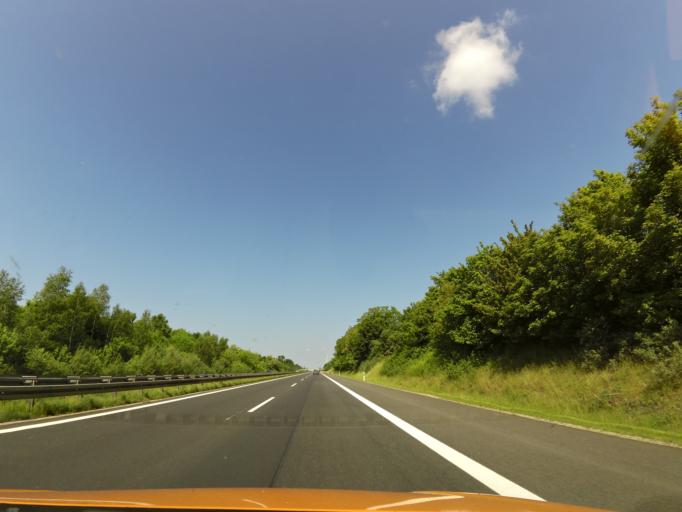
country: DE
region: Brandenburg
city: Gerdshagen
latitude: 53.2197
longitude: 12.2343
